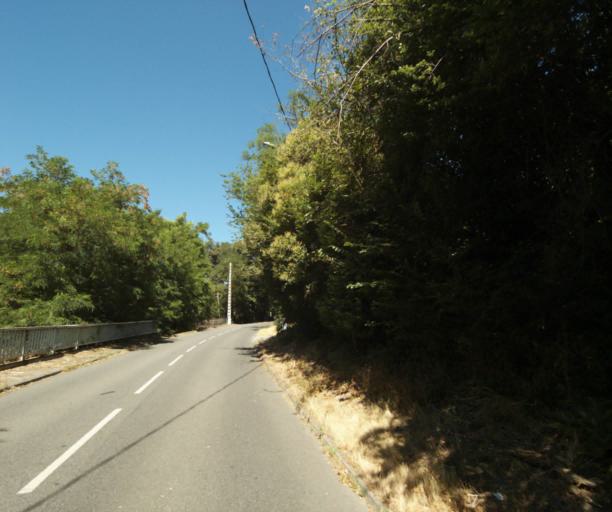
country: FR
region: Midi-Pyrenees
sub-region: Departement de la Haute-Garonne
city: Auzeville-Tolosane
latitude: 43.5142
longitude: 1.4809
